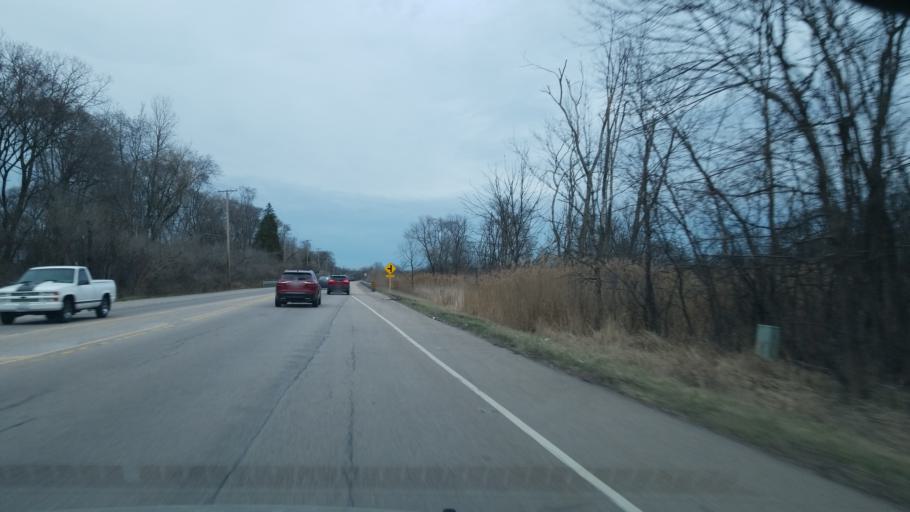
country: US
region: Illinois
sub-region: Kane County
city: Sleepy Hollow
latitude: 42.1033
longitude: -88.3308
